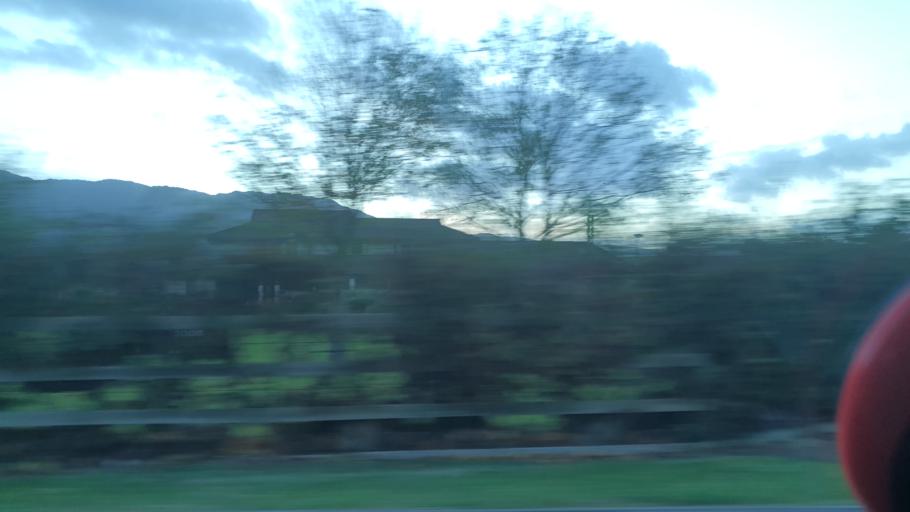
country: GB
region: Northern Ireland
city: Rostrevor
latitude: 54.0772
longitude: -6.1824
